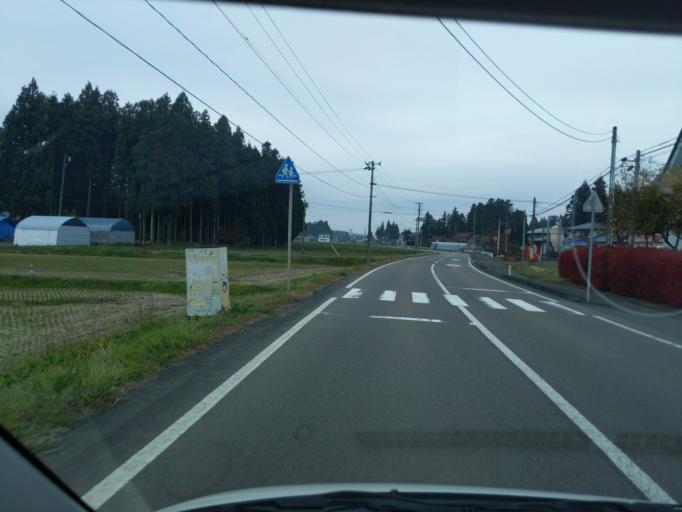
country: JP
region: Iwate
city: Mizusawa
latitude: 39.0980
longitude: 141.0897
